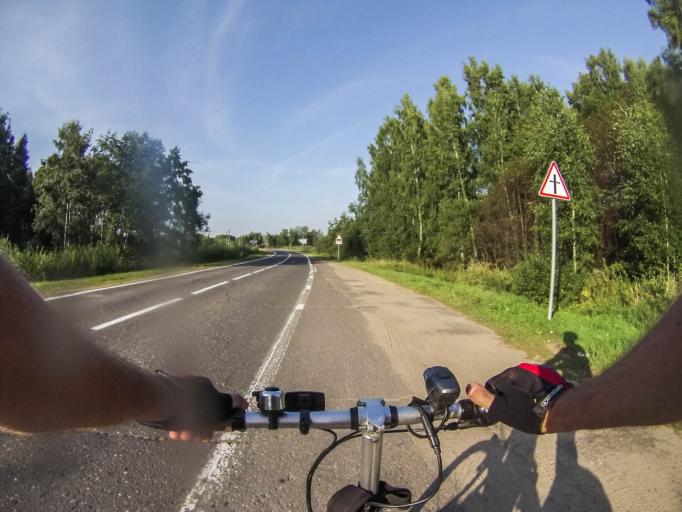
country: RU
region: Jaroslavl
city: Myshkin
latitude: 57.7268
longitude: 38.4208
